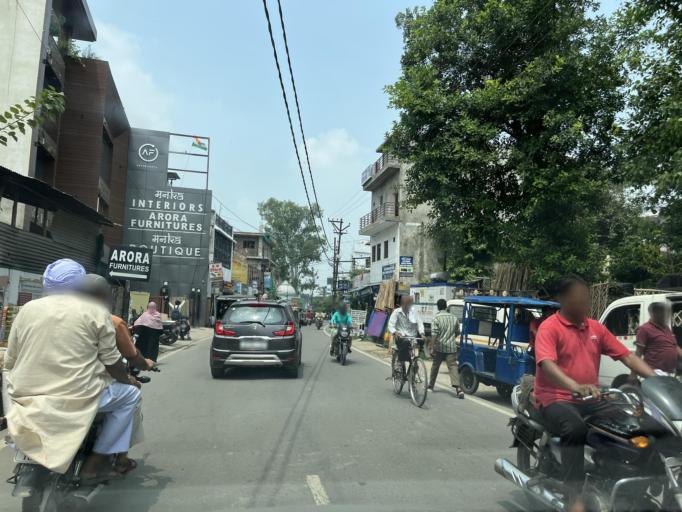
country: IN
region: Uttar Pradesh
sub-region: Bijnor
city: Najibabad
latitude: 29.6071
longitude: 78.3375
